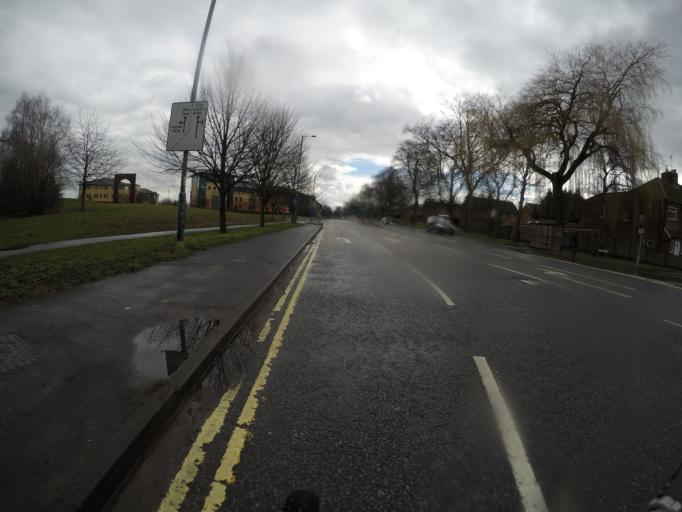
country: GB
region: England
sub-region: City of York
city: York
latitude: 53.9594
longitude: -1.1115
